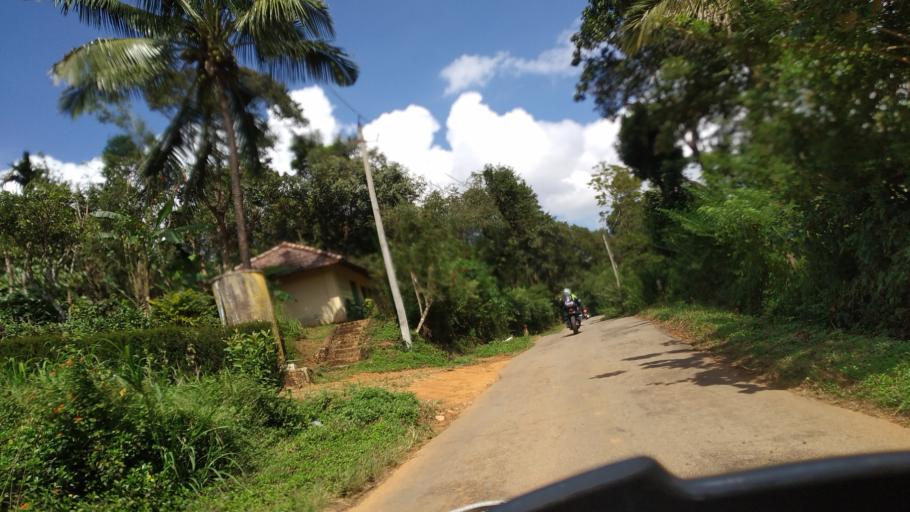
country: IN
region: Karnataka
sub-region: Kodagu
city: Ponnampet
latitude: 12.0326
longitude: 75.9010
